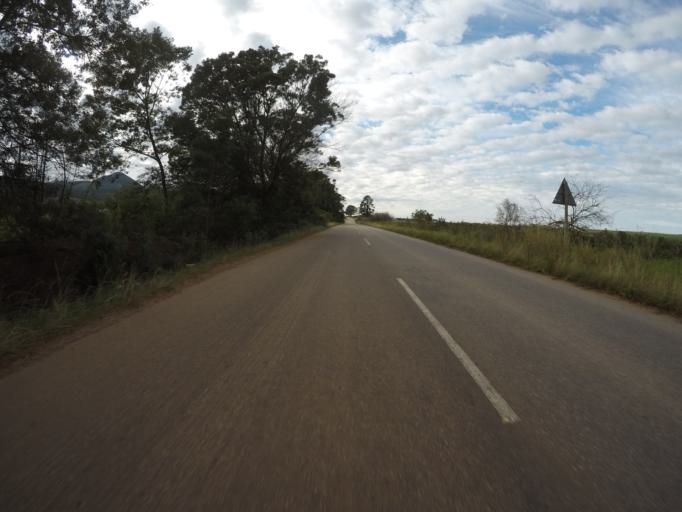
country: ZA
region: Eastern Cape
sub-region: Cacadu District Municipality
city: Kareedouw
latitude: -34.0091
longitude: 24.2692
